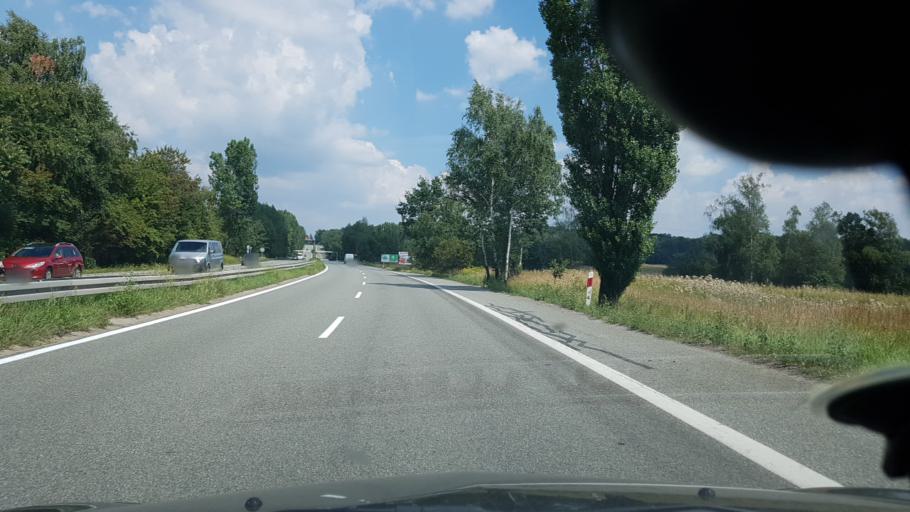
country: PL
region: Silesian Voivodeship
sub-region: Powiat mikolowski
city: Laziska Gorne
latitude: 50.1410
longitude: 18.8415
